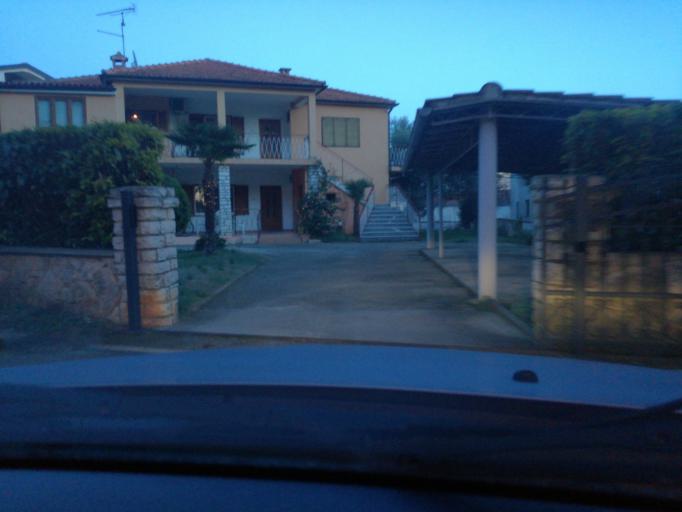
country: HR
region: Istarska
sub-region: Grad Rovinj
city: Rovinj
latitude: 45.0849
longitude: 13.6451
